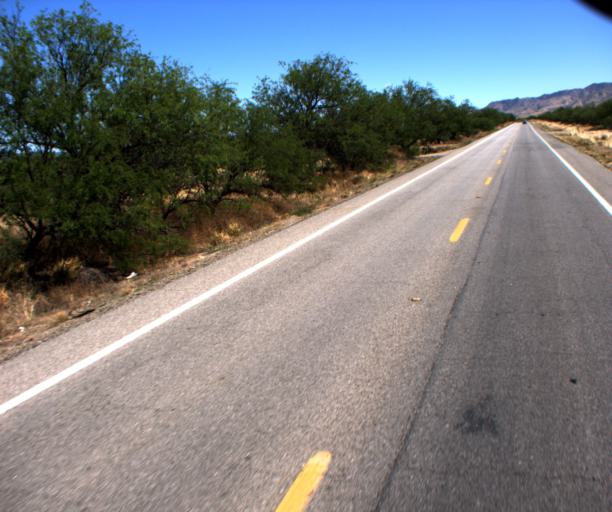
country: US
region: Arizona
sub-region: Santa Cruz County
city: Nogales
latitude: 31.4089
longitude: -110.8626
